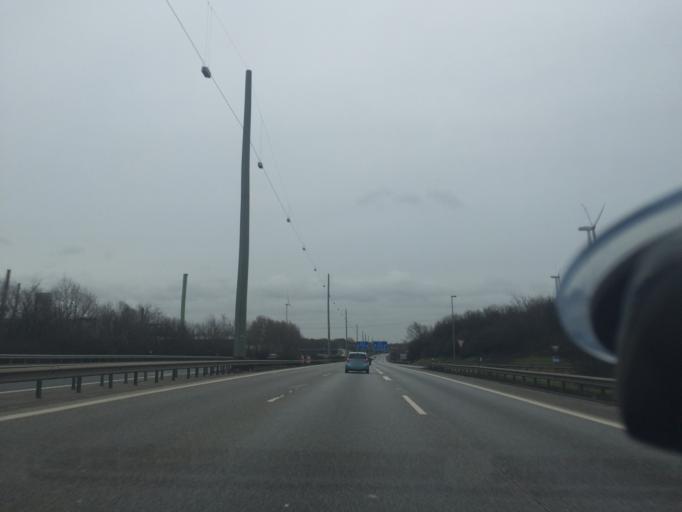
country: DE
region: Hamburg
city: Rothenburgsort
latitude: 53.5162
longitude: 10.0298
